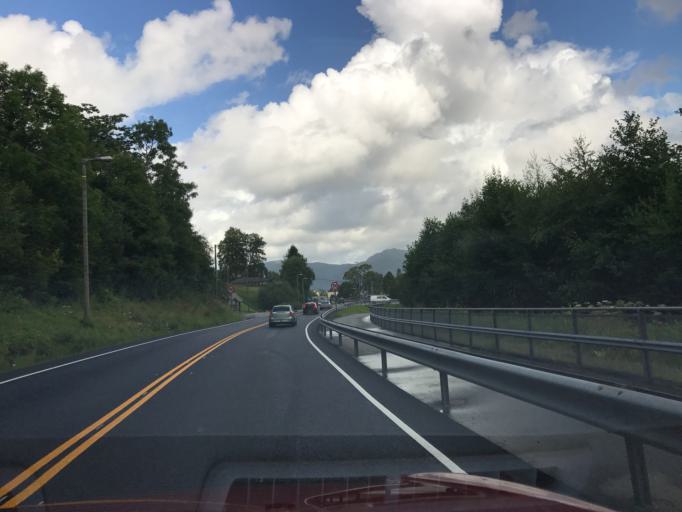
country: NO
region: Hordaland
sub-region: Bergen
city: Sandsli
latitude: 60.3091
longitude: 5.3625
